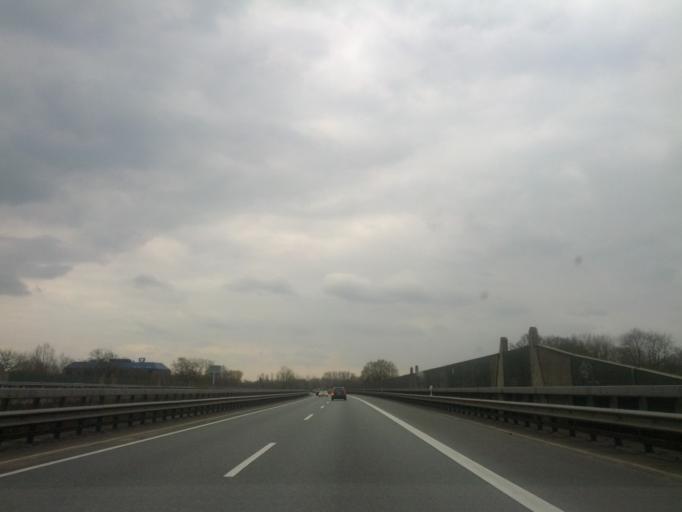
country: DE
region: Lower Saxony
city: Oldenburg
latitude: 53.1358
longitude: 8.1917
